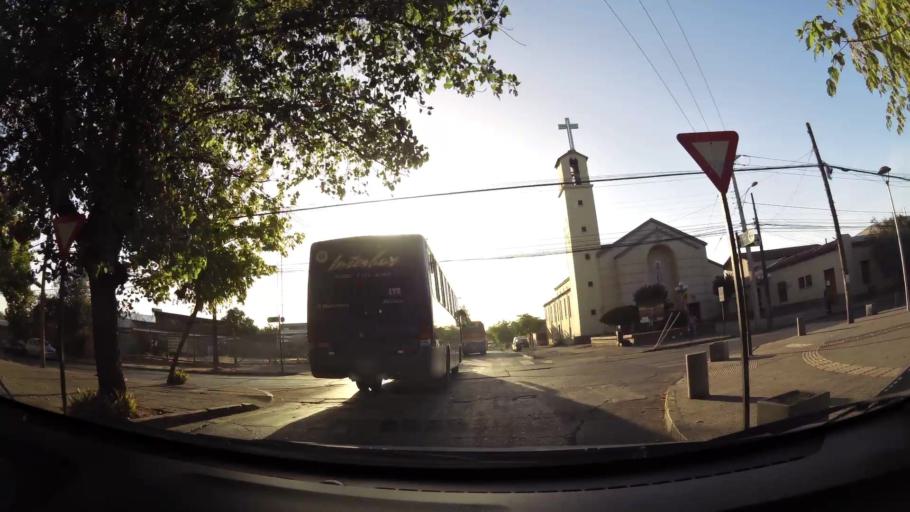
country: CL
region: Maule
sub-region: Provincia de Talca
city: Talca
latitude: -35.4319
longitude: -71.6455
